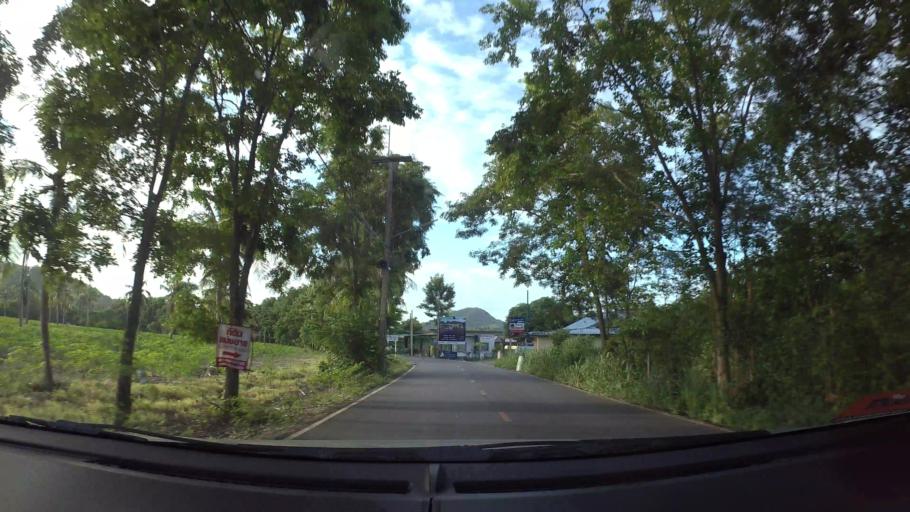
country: TH
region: Chon Buri
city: Sattahip
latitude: 12.7380
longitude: 100.9380
